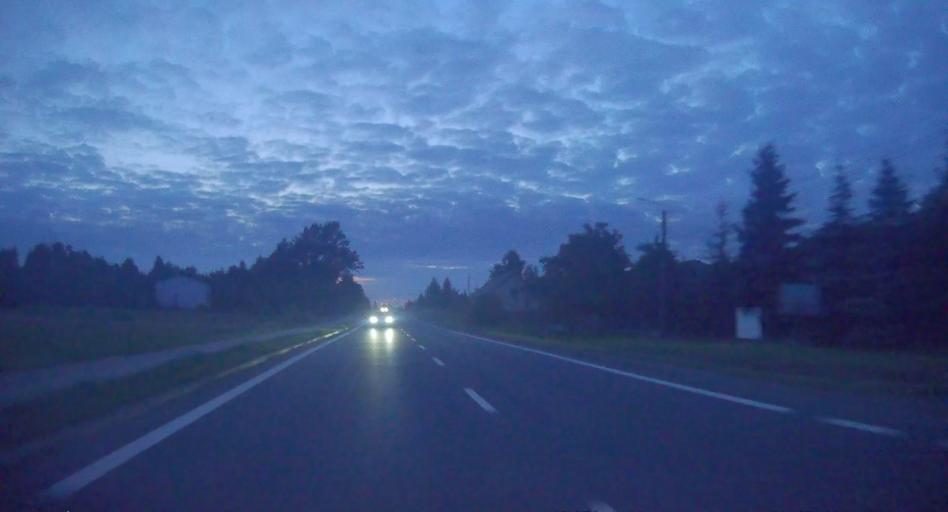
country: PL
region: Silesian Voivodeship
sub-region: Powiat klobucki
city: Kamyk
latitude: 50.8718
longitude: 19.0074
